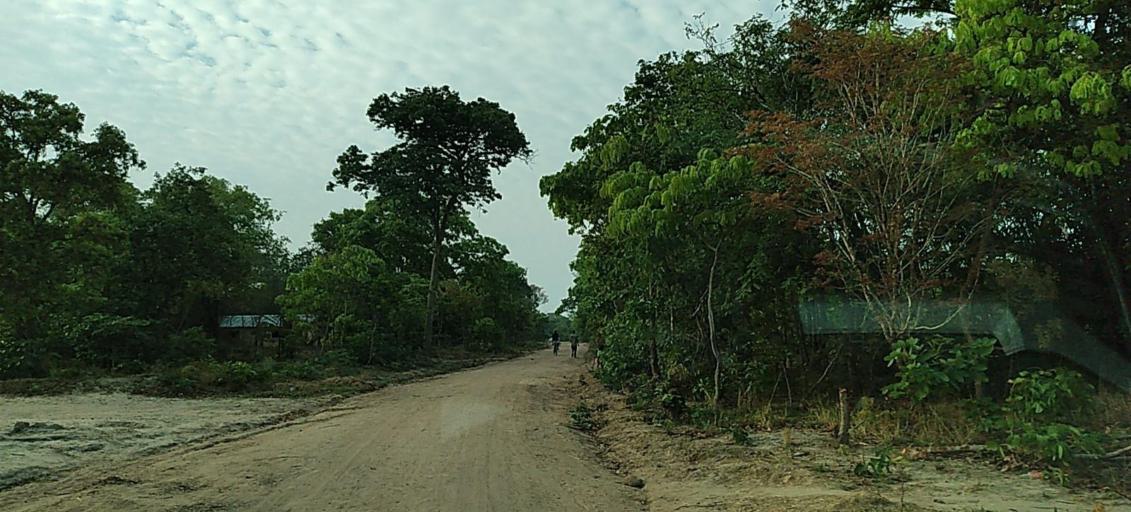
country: ZM
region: Copperbelt
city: Kalulushi
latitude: -12.8995
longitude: 27.6860
